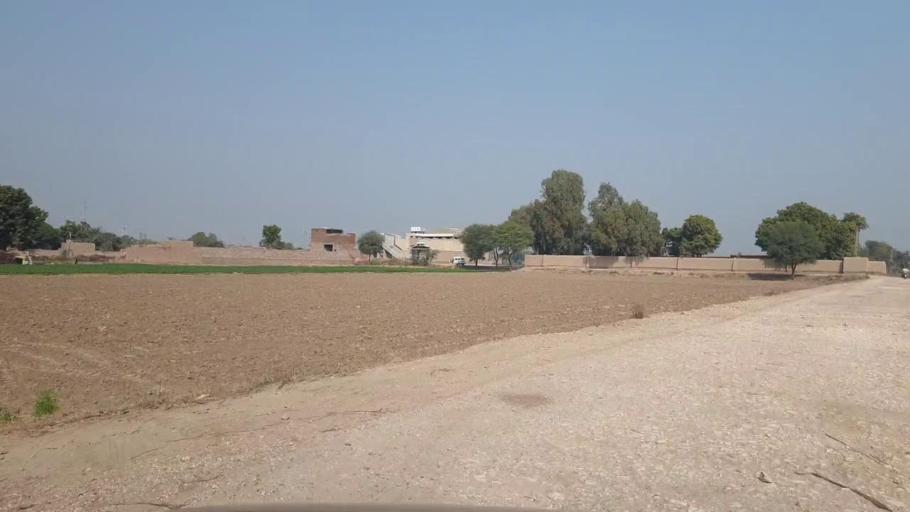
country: PK
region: Sindh
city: Bhit Shah
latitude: 25.7979
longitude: 68.4960
